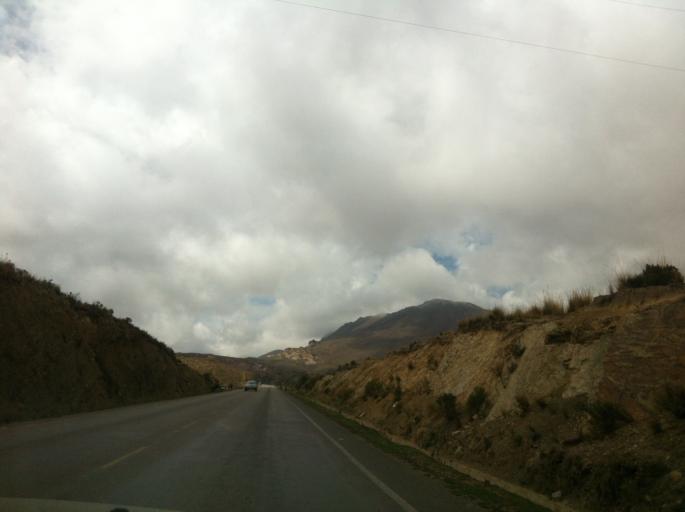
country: BO
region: Cochabamba
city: Irpa Irpa
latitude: -17.6812
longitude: -66.4828
